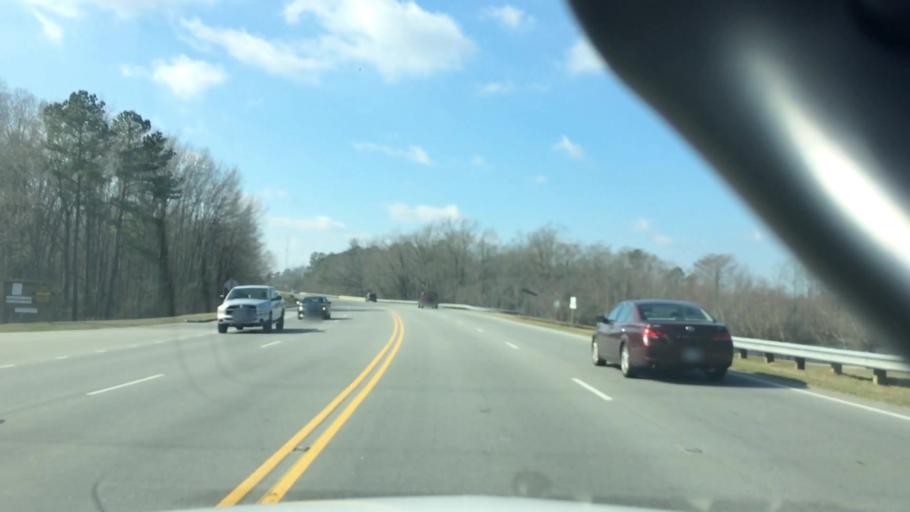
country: US
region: North Carolina
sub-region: Lenoir County
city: Kinston
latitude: 35.2586
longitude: -77.5916
